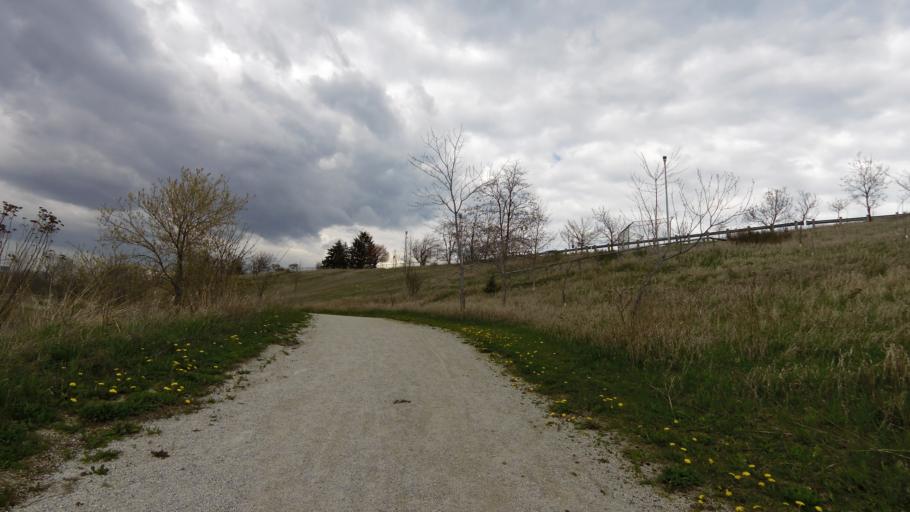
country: CA
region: Ontario
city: Mississauga
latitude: 43.6684
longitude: -79.6562
